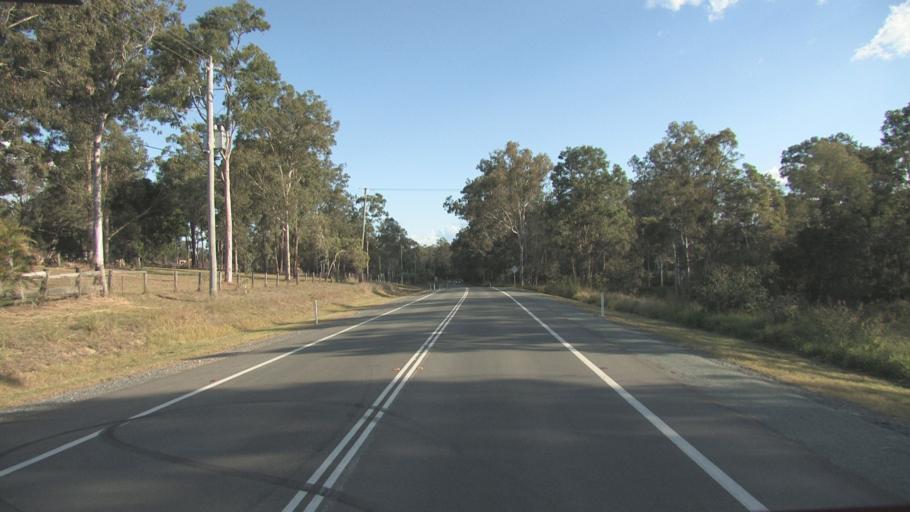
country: AU
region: Queensland
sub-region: Ipswich
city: Springfield Lakes
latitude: -27.7245
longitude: 152.9578
